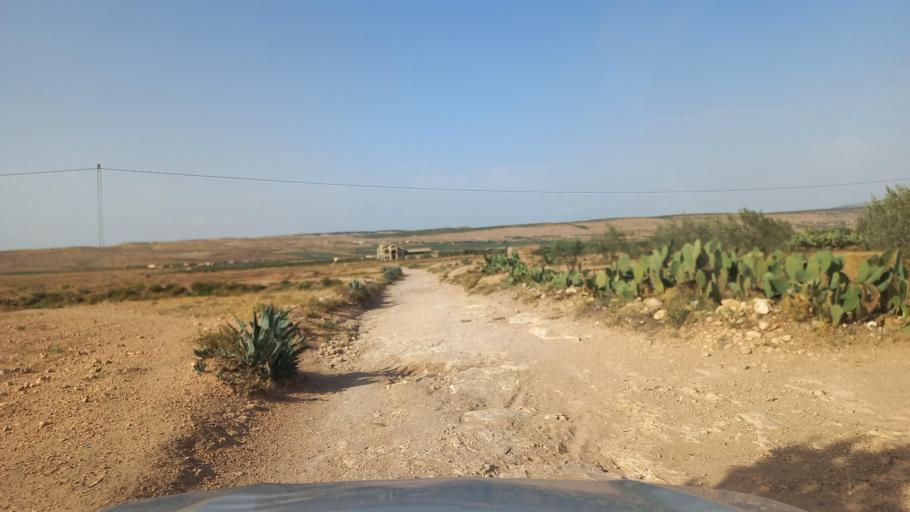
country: TN
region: Al Qasrayn
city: Kasserine
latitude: 35.3396
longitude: 8.8451
